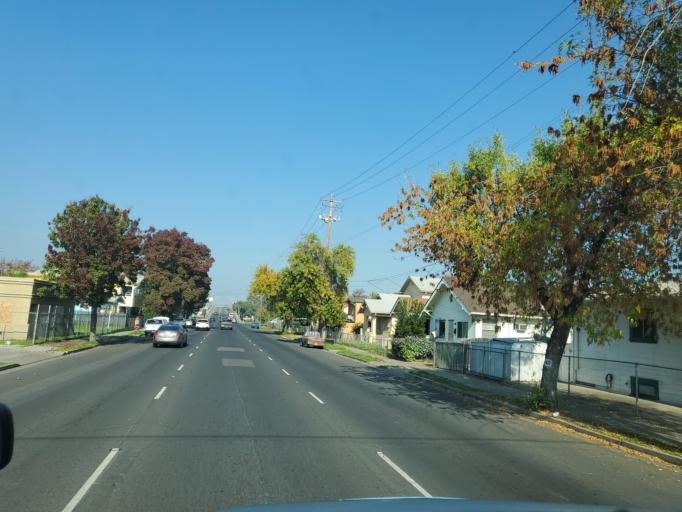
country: US
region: California
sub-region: San Joaquin County
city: Stockton
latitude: 37.9409
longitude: -121.2866
